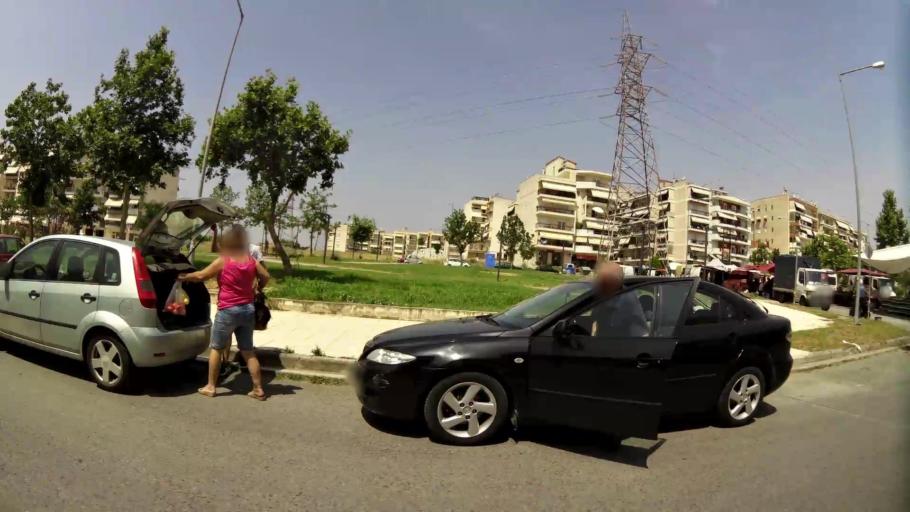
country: GR
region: Central Macedonia
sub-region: Nomos Thessalonikis
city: Evosmos
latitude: 40.6739
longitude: 22.9030
